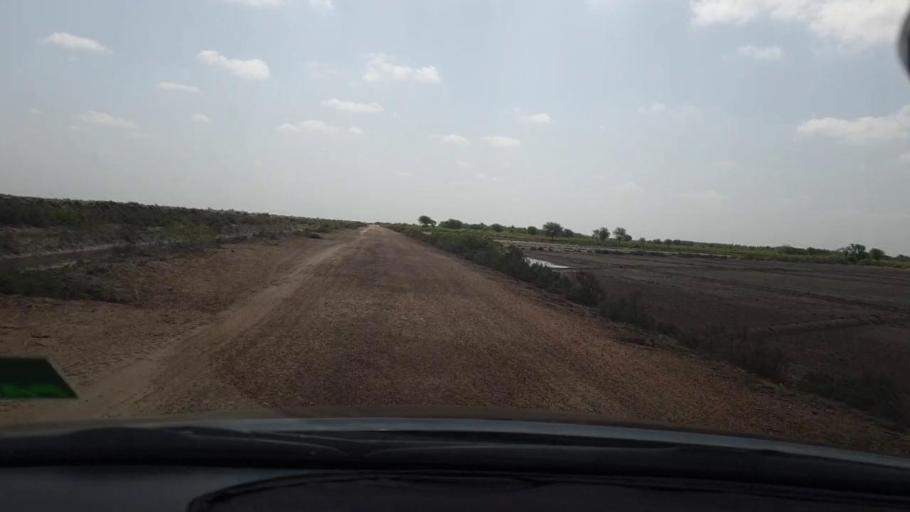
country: PK
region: Sindh
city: Tando Bago
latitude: 24.8365
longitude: 69.0504
